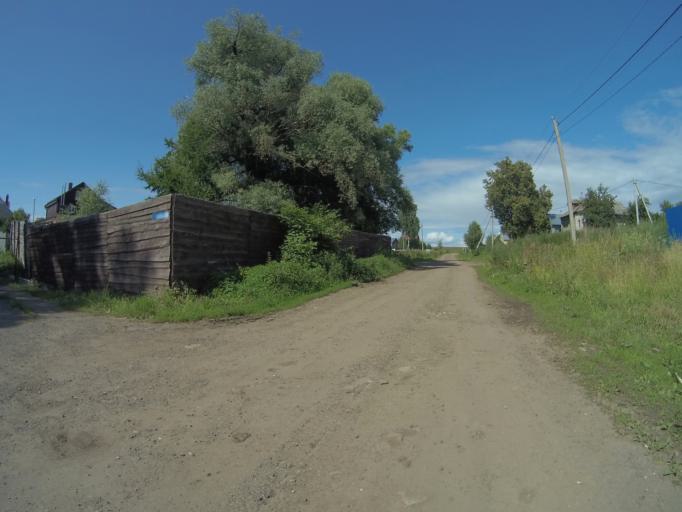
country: RU
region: Vladimir
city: Vladimir
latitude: 56.2699
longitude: 40.3727
